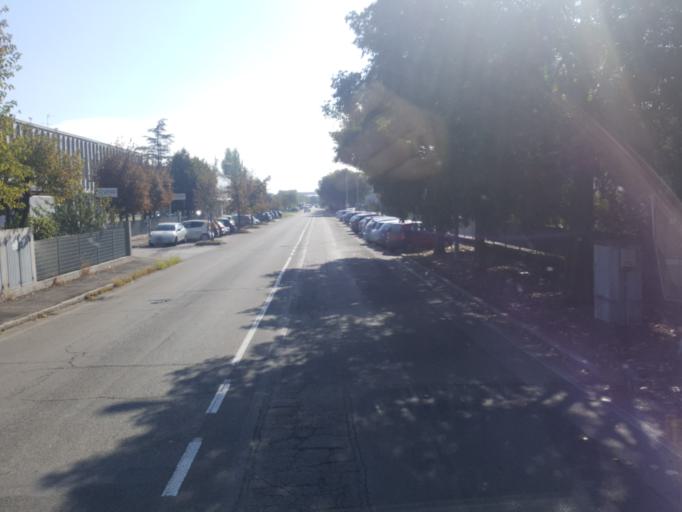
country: IT
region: Emilia-Romagna
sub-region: Provincia di Modena
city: Villanova
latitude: 44.6715
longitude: 10.9310
